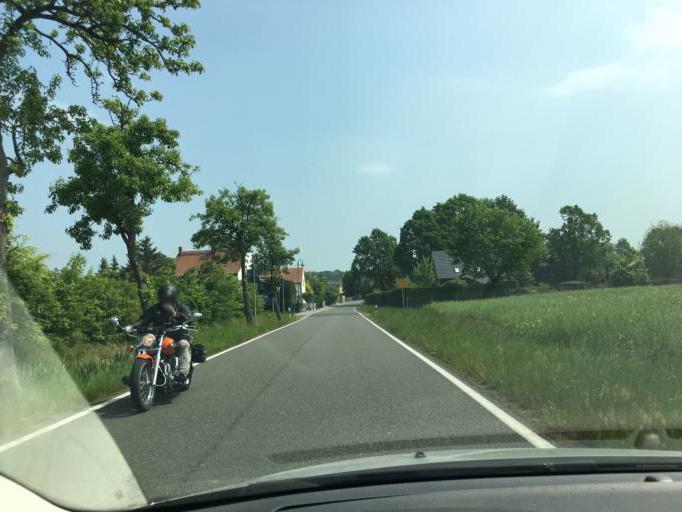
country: DE
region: Saxony
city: Naunhof
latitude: 51.2732
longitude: 12.6310
